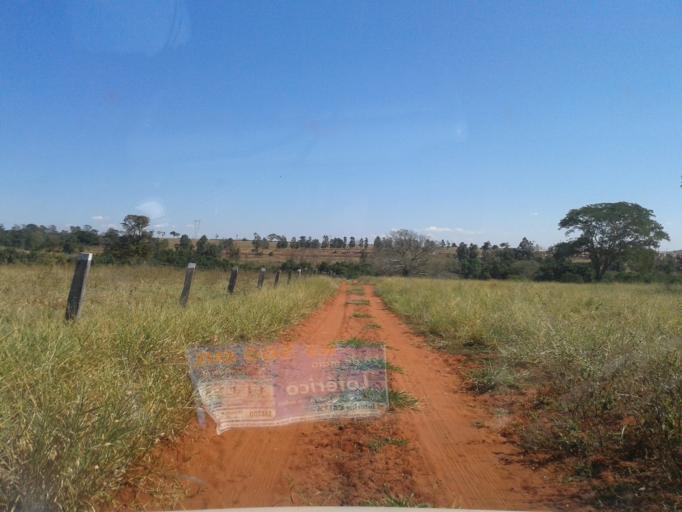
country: BR
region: Minas Gerais
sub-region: Santa Vitoria
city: Santa Vitoria
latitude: -19.0738
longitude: -50.3596
